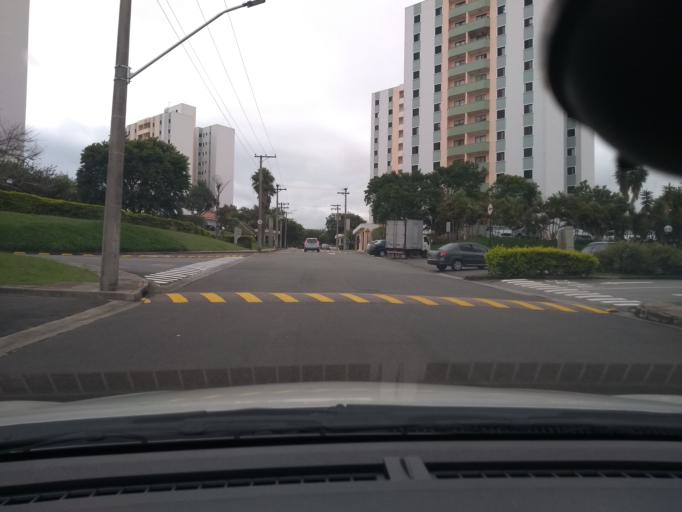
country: BR
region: Sao Paulo
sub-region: Jundiai
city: Jundiai
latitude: -23.1888
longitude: -46.9582
